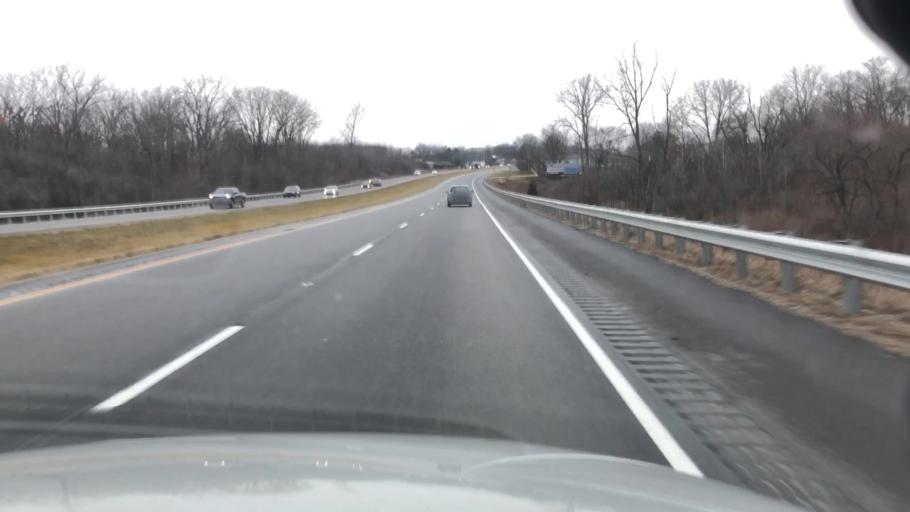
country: US
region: Indiana
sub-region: Kosciusko County
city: Pierceton
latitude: 41.1975
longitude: -85.6896
